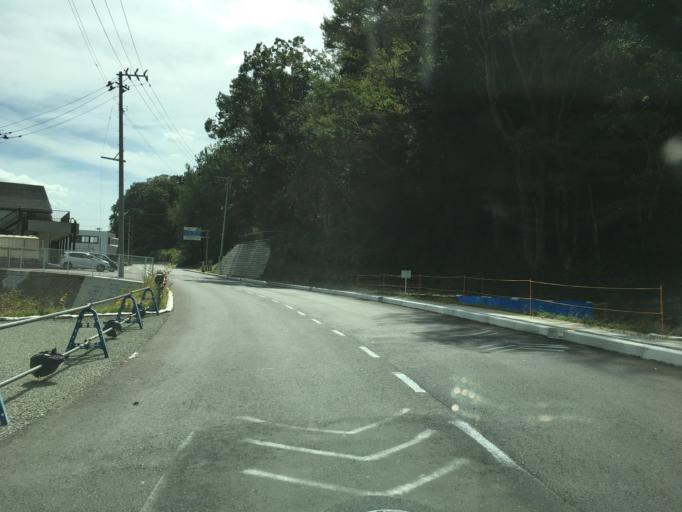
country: JP
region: Fukushima
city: Nihommatsu
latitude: 37.5935
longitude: 140.4248
